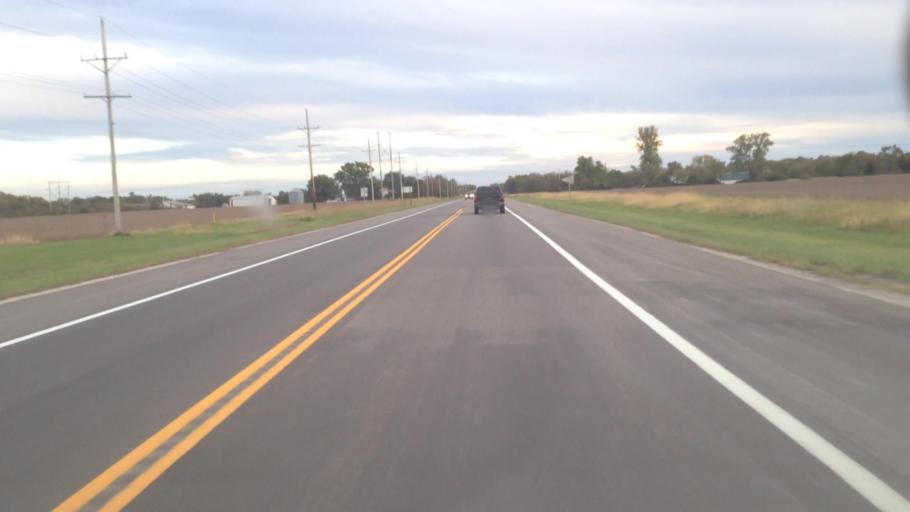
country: US
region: Kansas
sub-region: Franklin County
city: Ottawa
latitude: 38.5645
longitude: -95.2679
